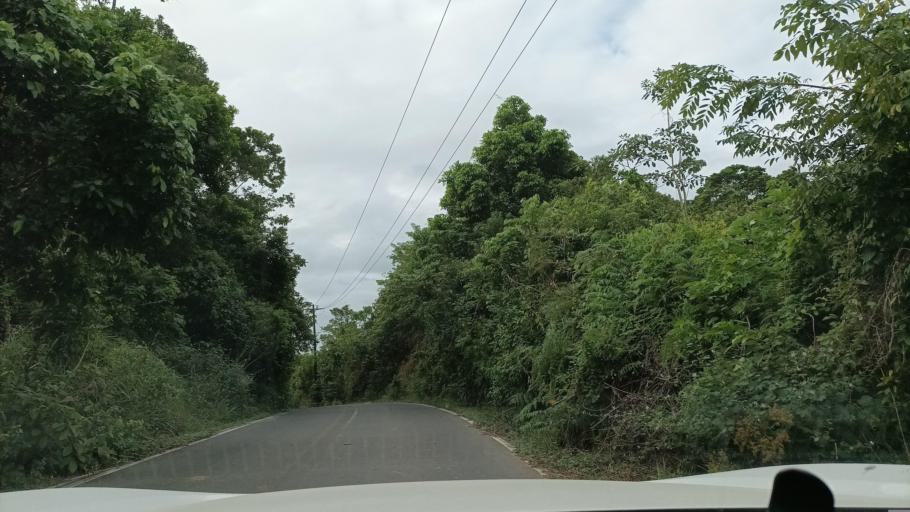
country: MX
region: Veracruz
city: Hidalgotitlan
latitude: 17.6880
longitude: -94.4518
